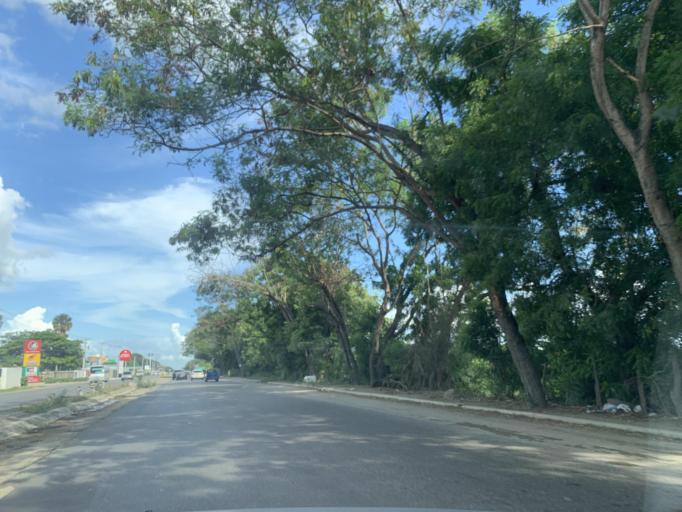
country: DO
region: Santiago
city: Villa Gonzalez
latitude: 19.5453
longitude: -70.8048
